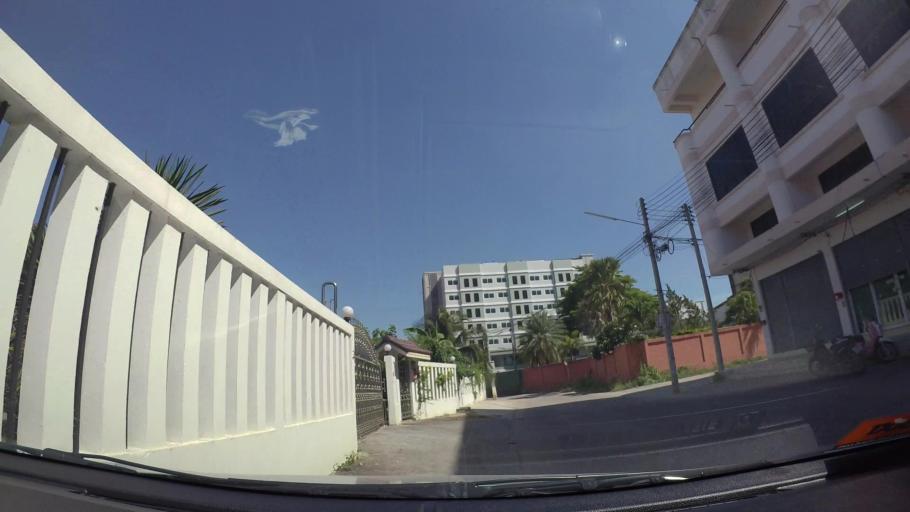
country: TH
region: Chon Buri
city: Si Racha
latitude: 13.1609
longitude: 100.9342
